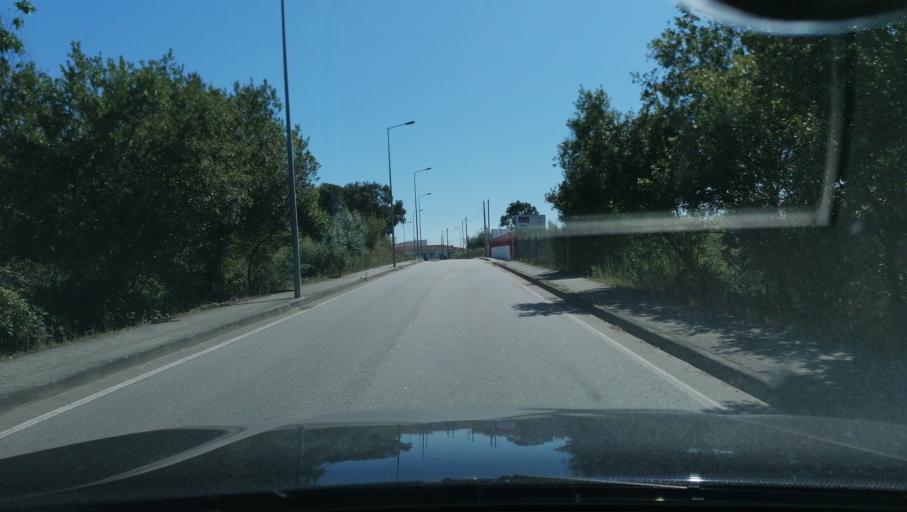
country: PT
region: Porto
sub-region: Vila Nova de Gaia
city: Vila Nova da Telha
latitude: 41.0756
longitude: -8.6427
